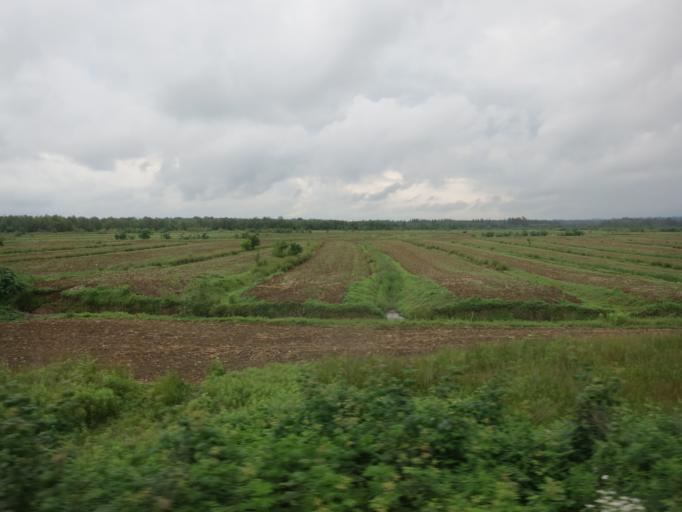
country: GE
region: Ajaria
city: Ochkhamuri
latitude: 41.8770
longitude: 41.8265
